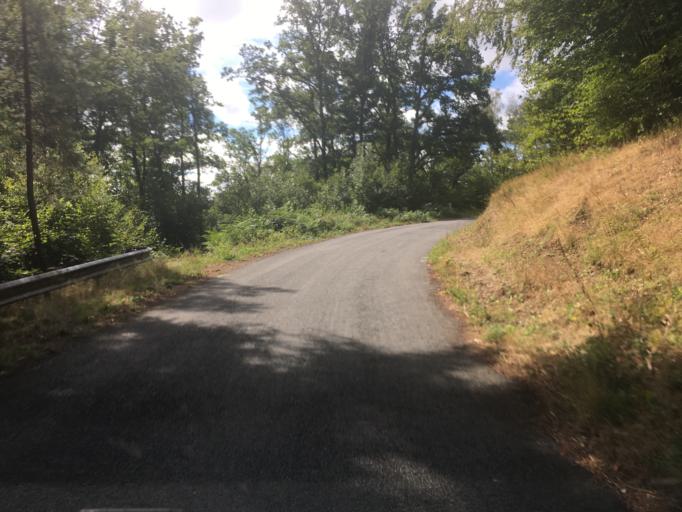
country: FR
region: Auvergne
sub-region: Departement du Cantal
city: Champagnac
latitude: 45.4237
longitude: 2.3929
